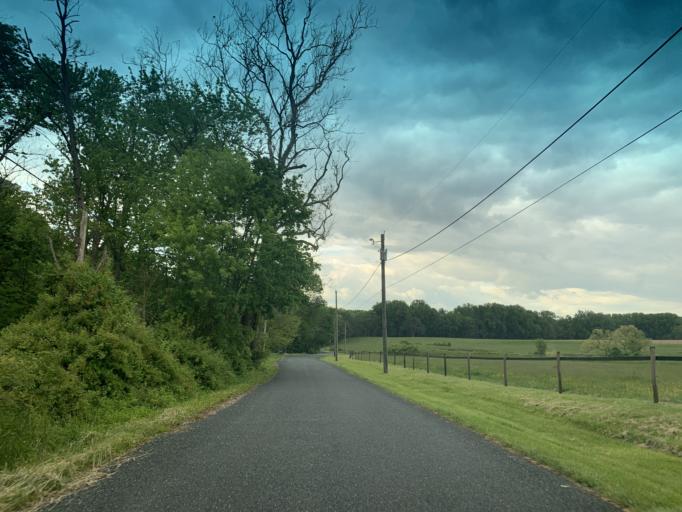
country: US
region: Maryland
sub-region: Cecil County
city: Rising Sun
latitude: 39.6638
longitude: -76.2072
